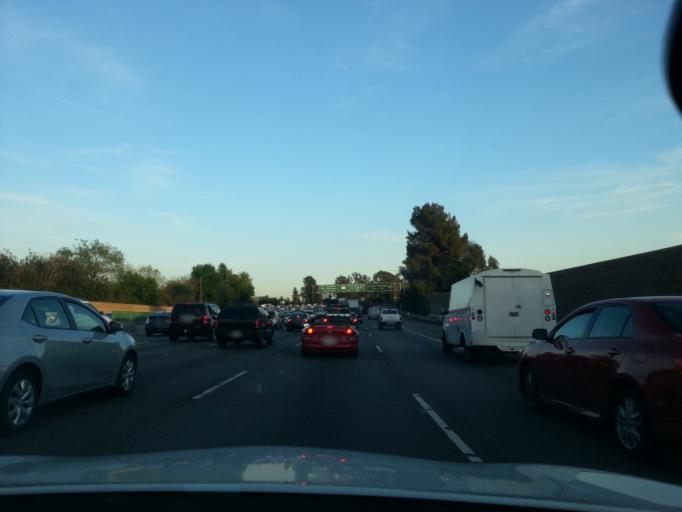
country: US
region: California
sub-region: Los Angeles County
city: North Hollywood
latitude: 34.1559
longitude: -118.4019
